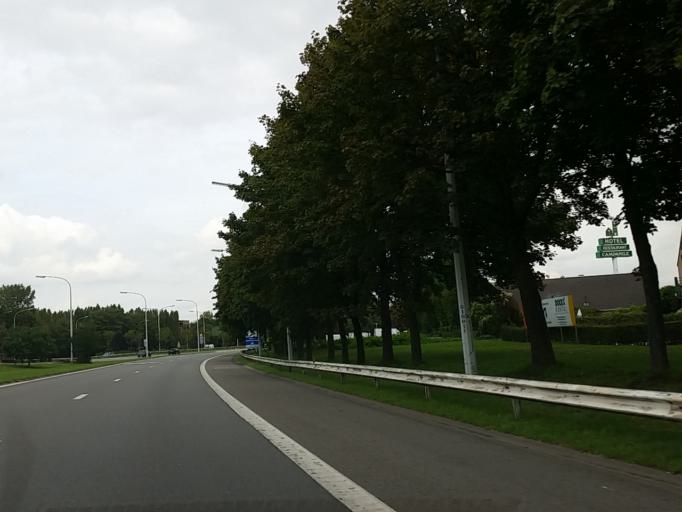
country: BE
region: Flanders
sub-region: Provincie Vlaams-Brabant
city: Drogenbos
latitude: 50.8099
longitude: 4.3019
